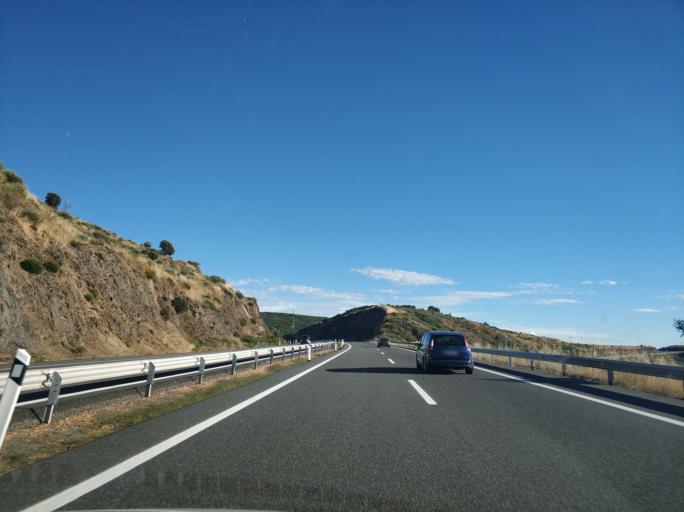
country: ES
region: Castille and Leon
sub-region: Provincia de Leon
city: Carrocera
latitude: 42.7564
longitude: -5.7733
